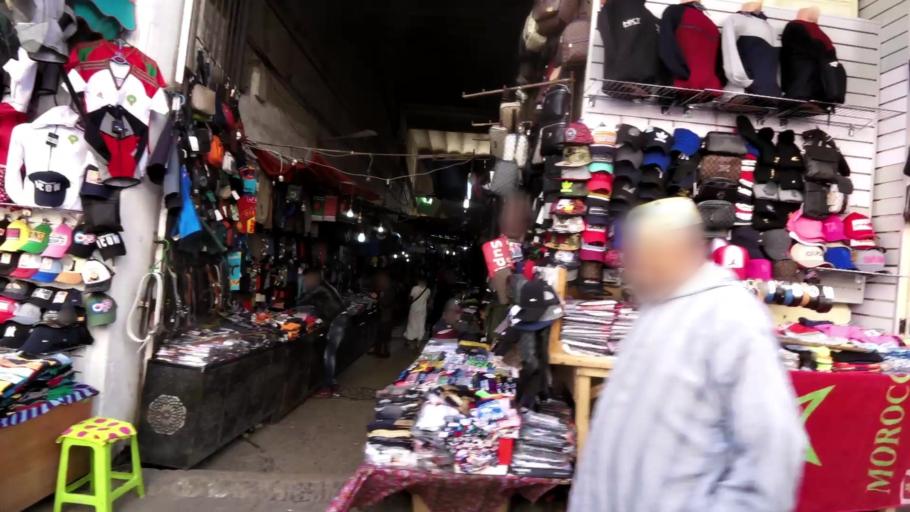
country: MA
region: Tanger-Tetouan
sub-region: Tanger-Assilah
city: Tangier
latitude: 35.7832
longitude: -5.8107
